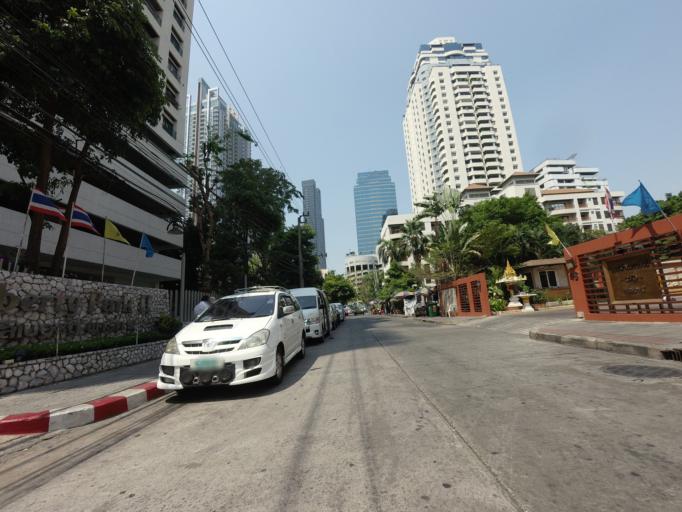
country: TH
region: Bangkok
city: Din Daeng
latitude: 13.7469
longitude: 100.5562
